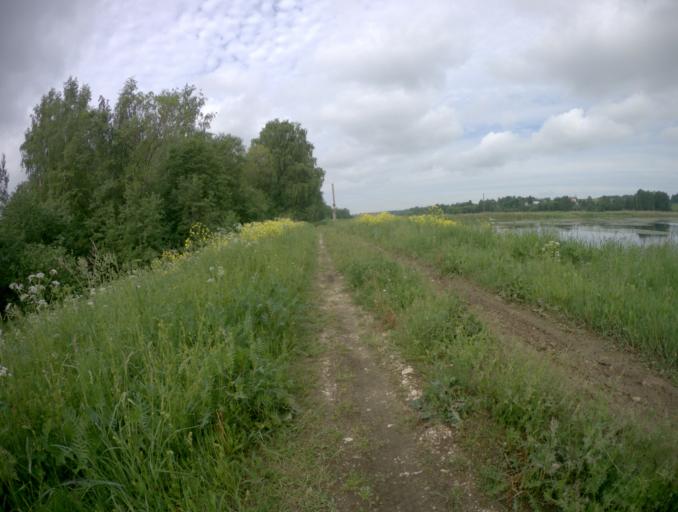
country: RU
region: Vladimir
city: Lakinsk
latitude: 56.0695
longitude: 39.9628
